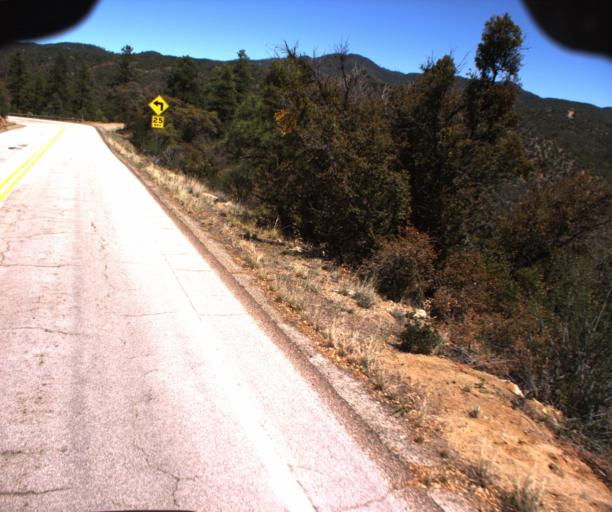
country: US
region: Arizona
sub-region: Yavapai County
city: Prescott
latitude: 34.4373
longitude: -112.5459
